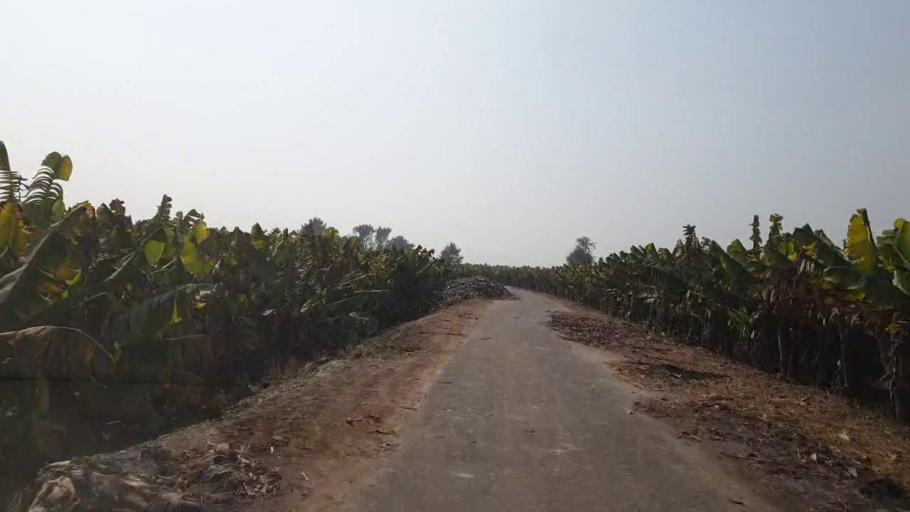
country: PK
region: Sindh
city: Bhit Shah
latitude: 25.7786
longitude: 68.4822
